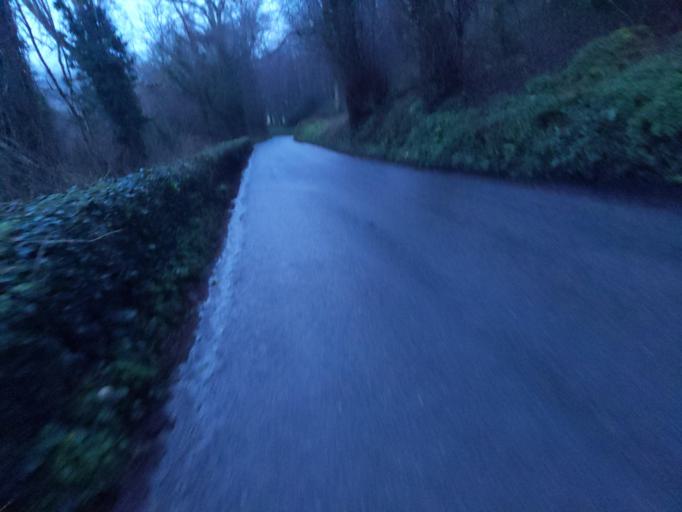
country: GB
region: England
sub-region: Devon
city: Yealmpton
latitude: 50.3379
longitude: -4.0132
